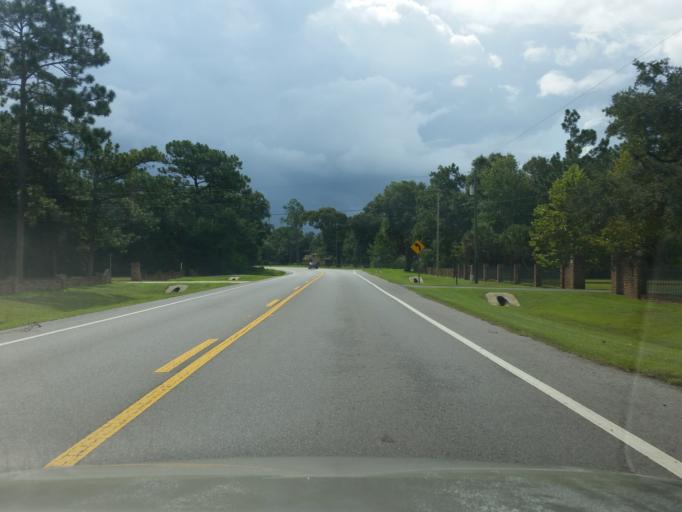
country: US
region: Florida
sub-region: Escambia County
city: Gonzalez
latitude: 30.5400
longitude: -87.3224
